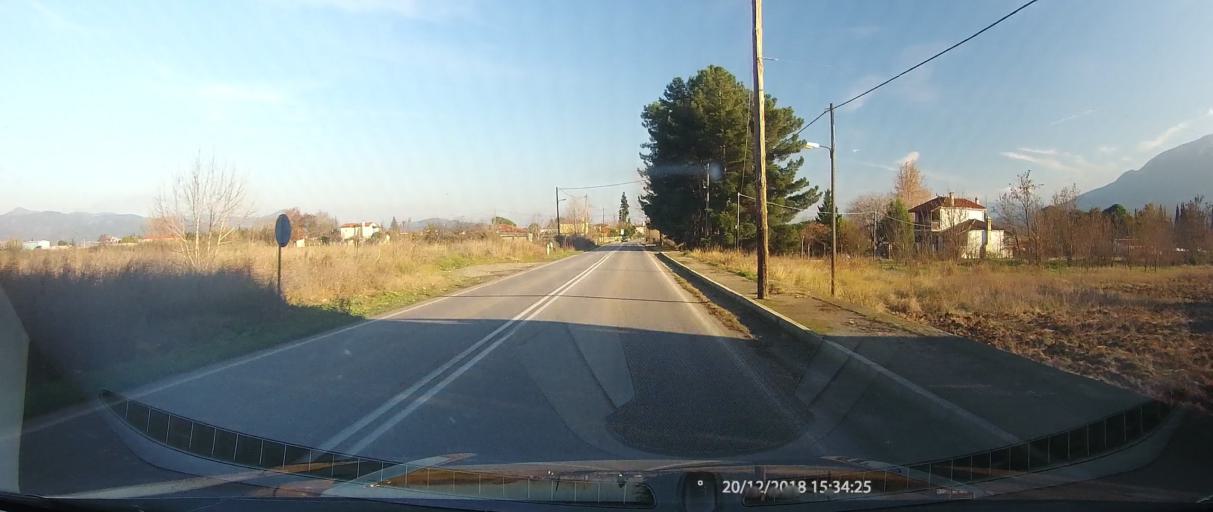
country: GR
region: Central Greece
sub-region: Nomos Fthiotidos
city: Lianokladhion
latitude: 38.9190
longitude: 22.2943
